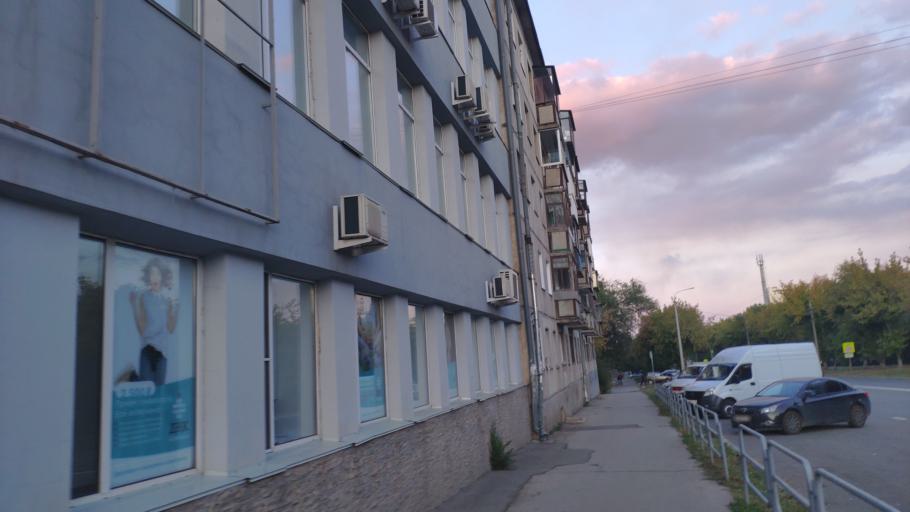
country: RU
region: Chelyabinsk
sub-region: Gorod Magnitogorsk
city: Magnitogorsk
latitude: 53.4118
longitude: 58.9726
